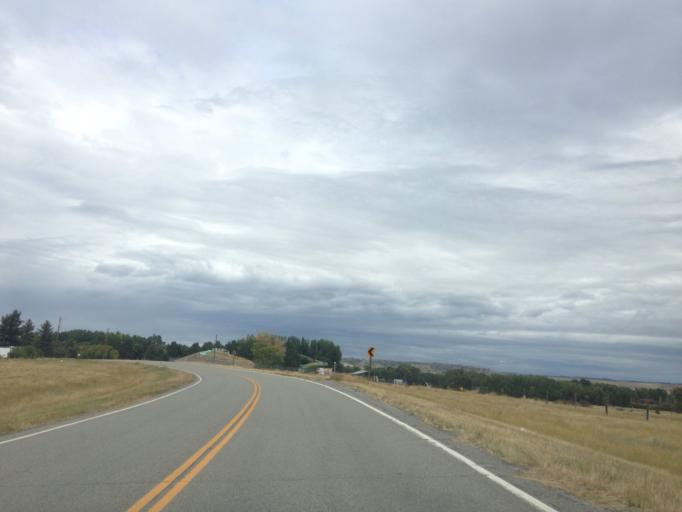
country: US
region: Montana
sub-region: Sweet Grass County
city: Big Timber
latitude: 45.7711
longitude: -109.7965
